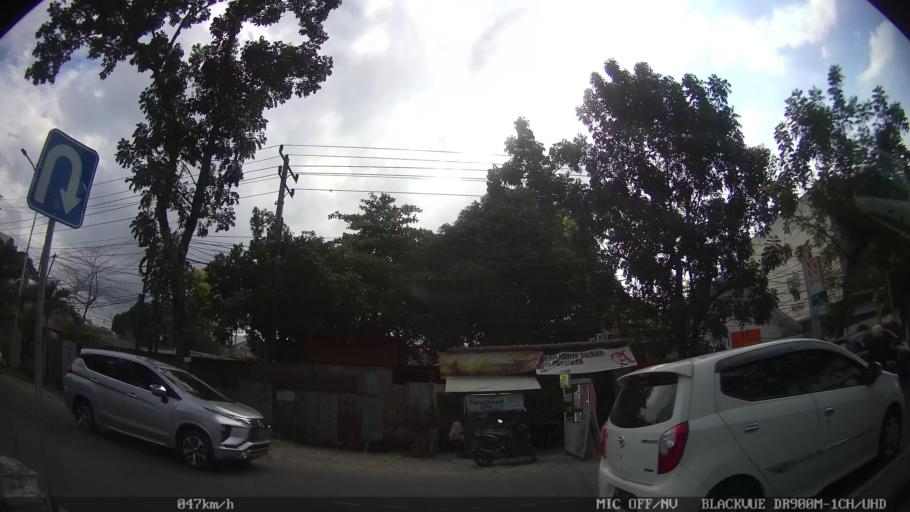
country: ID
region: North Sumatra
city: Medan
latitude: 3.6196
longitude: 98.6711
